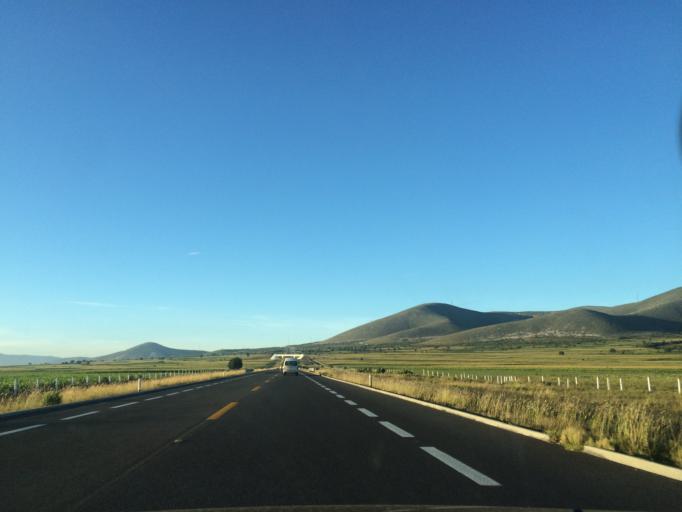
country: MX
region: Puebla
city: Morelos Canada
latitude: 18.7497
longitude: -97.4798
